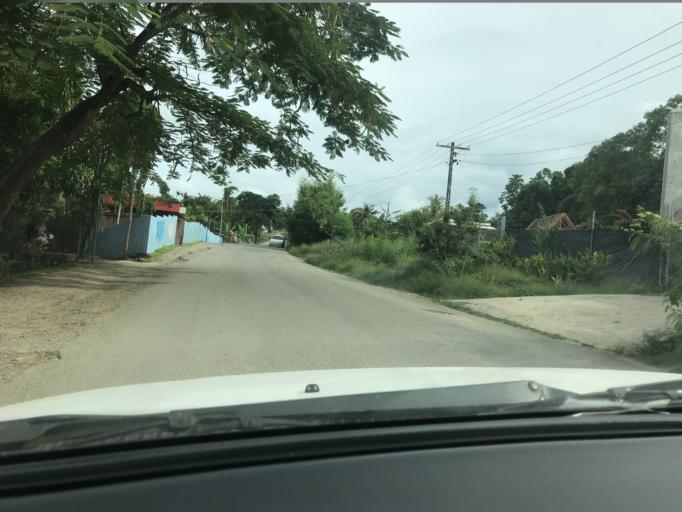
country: SB
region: Guadalcanal
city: Honiara
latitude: -9.4338
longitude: 159.9449
